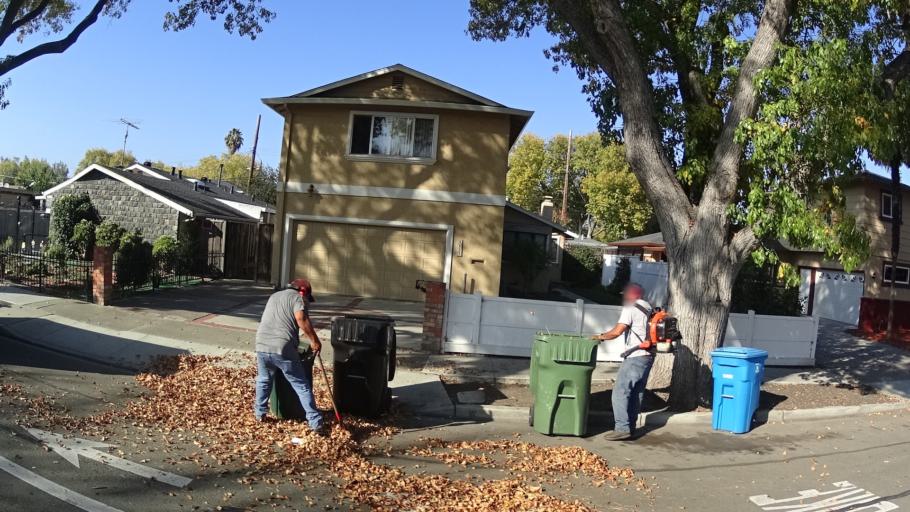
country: US
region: California
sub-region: Santa Clara County
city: Santa Clara
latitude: 37.3588
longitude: -121.9828
